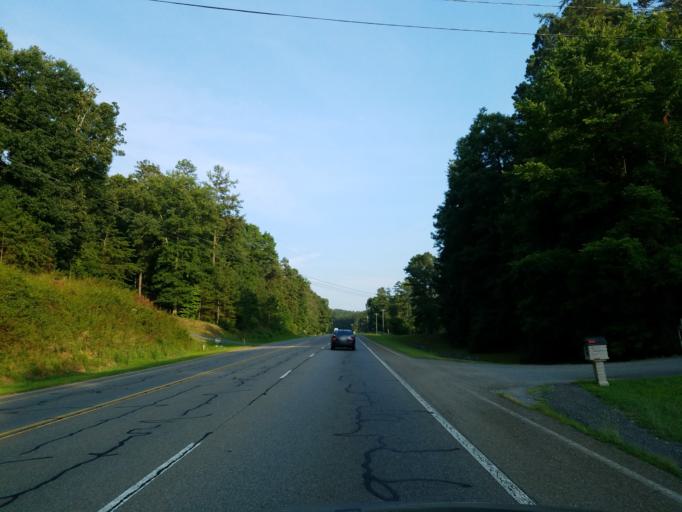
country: US
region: Georgia
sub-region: Gilmer County
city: Ellijay
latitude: 34.6634
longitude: -84.4490
